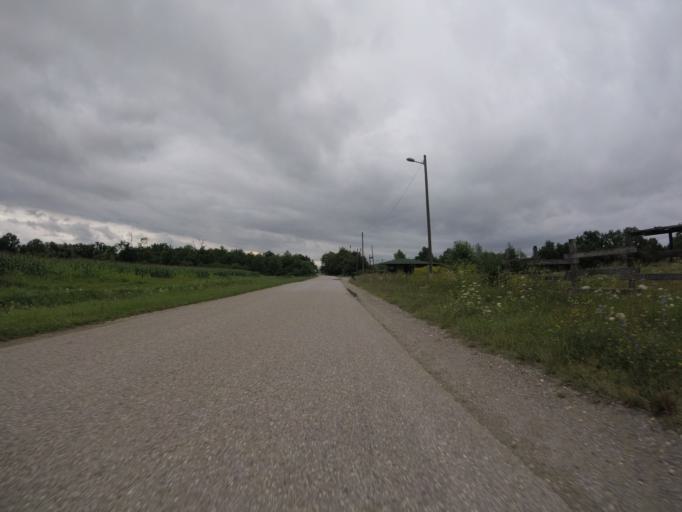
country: HR
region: Zagrebacka
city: Mraclin
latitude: 45.6596
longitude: 16.0997
